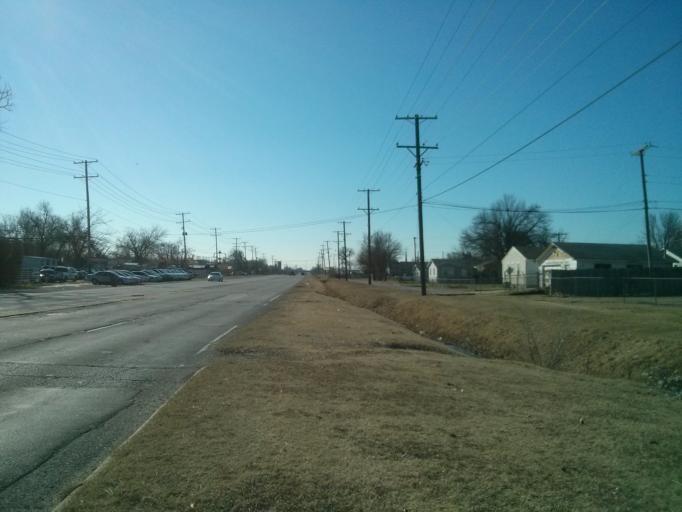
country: US
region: Oklahoma
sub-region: Tulsa County
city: Owasso
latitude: 36.1755
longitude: -95.8689
